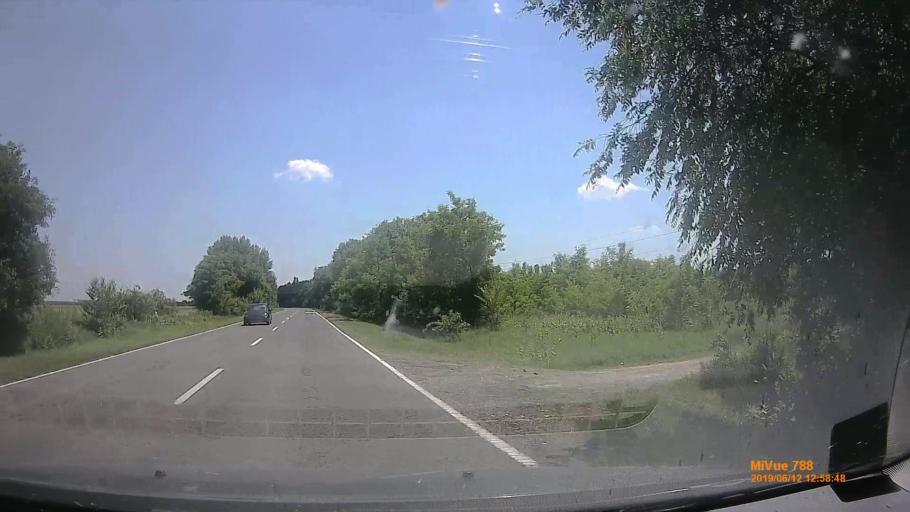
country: HU
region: Bacs-Kiskun
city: Palmonostora
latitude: 46.6180
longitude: 19.9036
